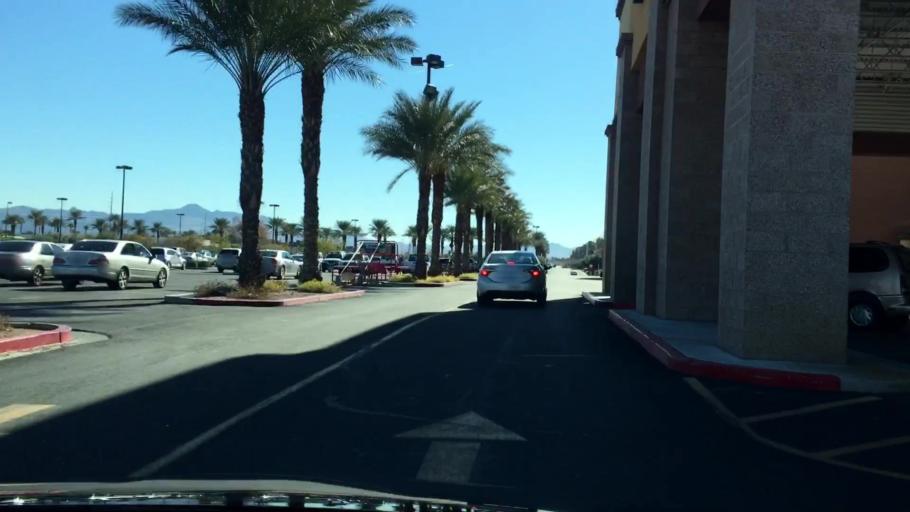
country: US
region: Nevada
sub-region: Clark County
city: Paradise
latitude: 36.0851
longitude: -115.1215
